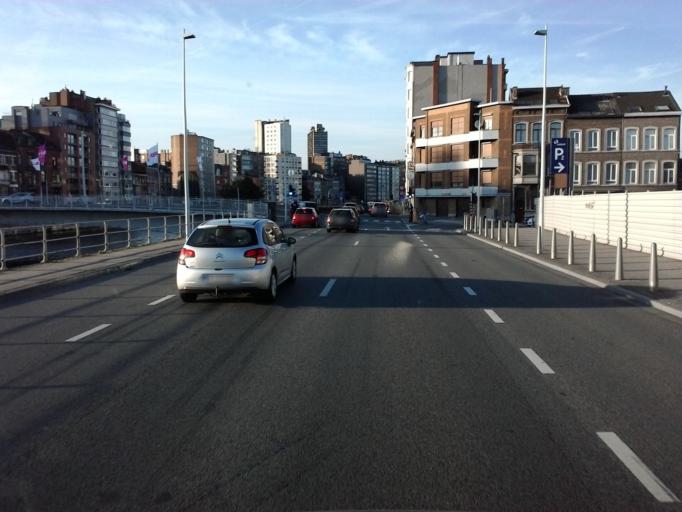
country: BE
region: Wallonia
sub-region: Province de Liege
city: Liege
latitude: 50.6323
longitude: 5.5782
